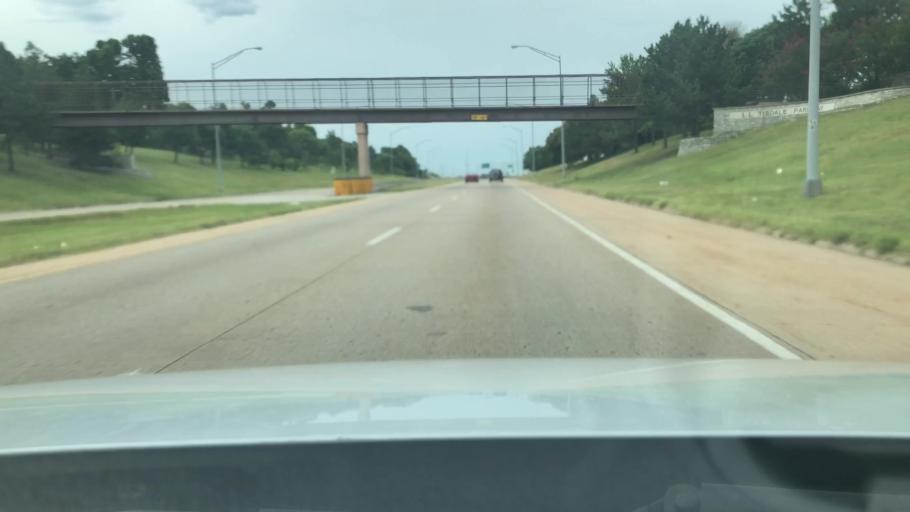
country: US
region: Oklahoma
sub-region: Tulsa County
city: Tulsa
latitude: 36.1695
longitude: -96.0008
